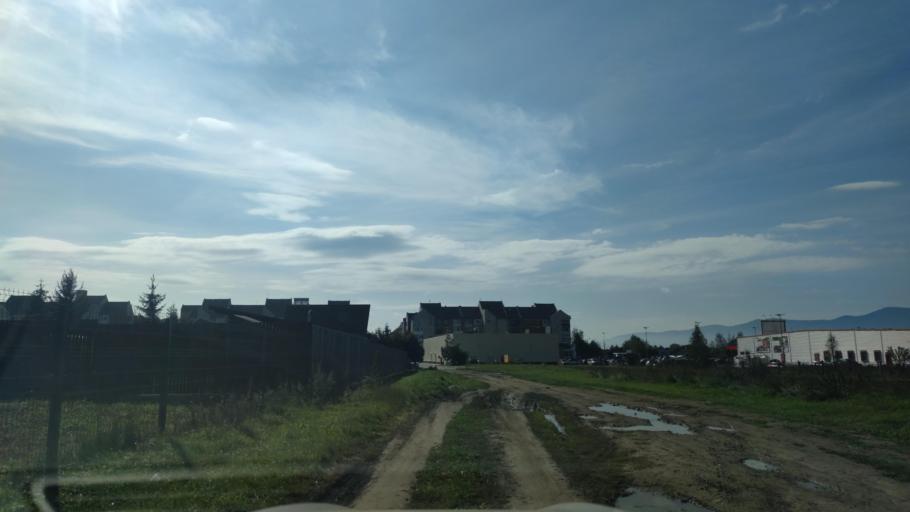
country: RO
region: Harghita
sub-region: Municipiul Gheorgheni
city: Gheorgheni
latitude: 46.7229
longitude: 25.5837
